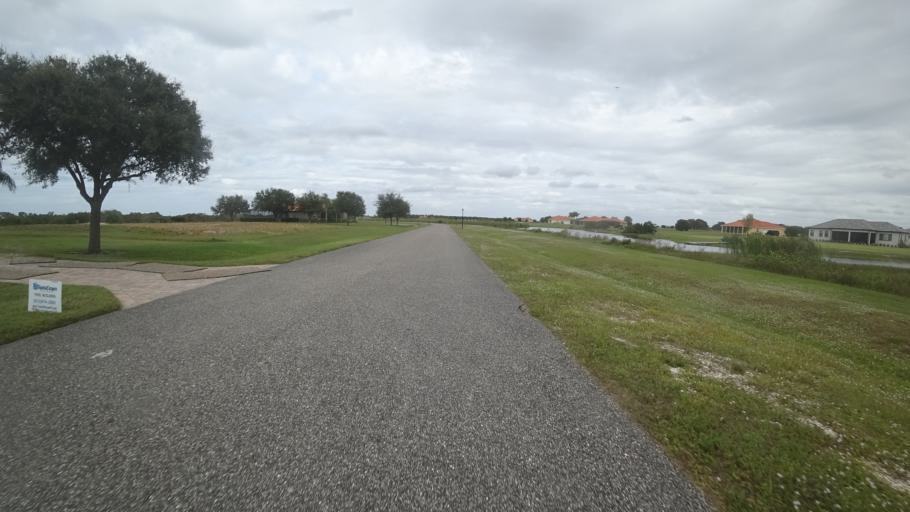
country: US
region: Florida
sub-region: Hillsborough County
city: Wimauma
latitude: 27.6492
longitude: -82.3303
